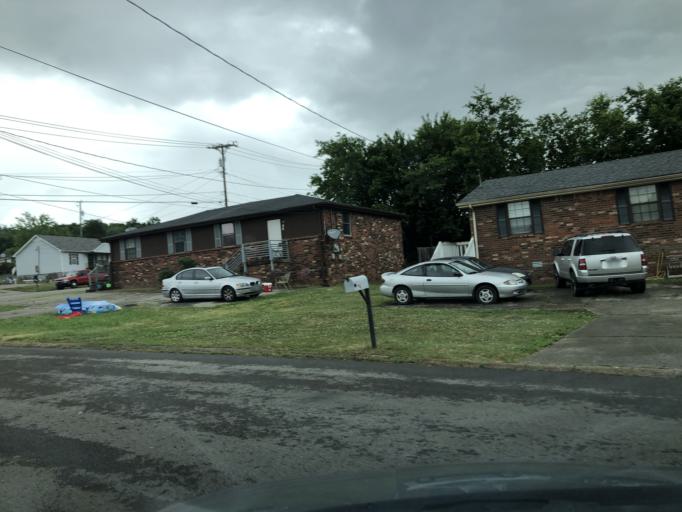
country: US
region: Tennessee
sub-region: Davidson County
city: Nashville
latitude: 36.2472
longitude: -86.7707
